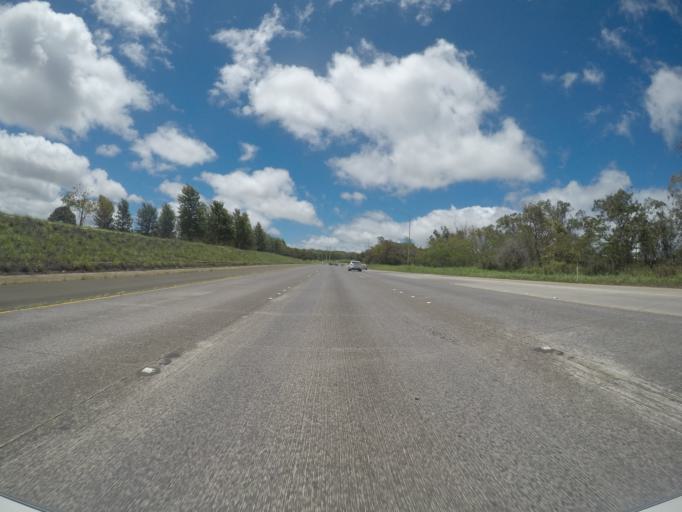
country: US
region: Hawaii
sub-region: Honolulu County
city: Mililani Town
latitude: 21.4387
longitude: -157.9938
